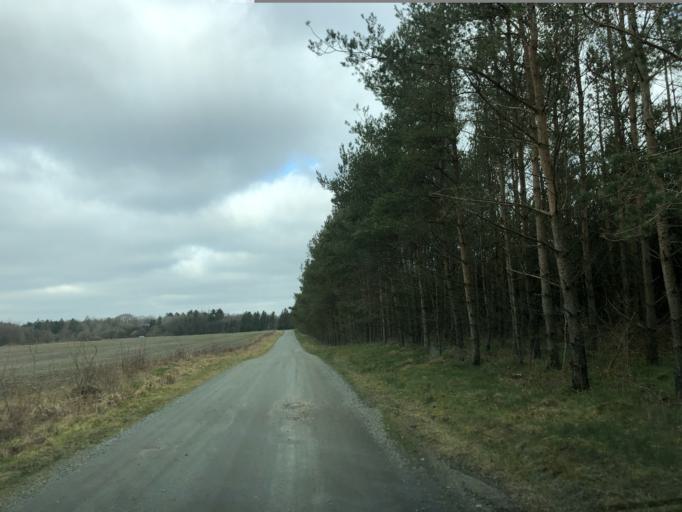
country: DK
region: South Denmark
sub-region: Billund Kommune
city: Billund
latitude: 55.7743
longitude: 9.1381
